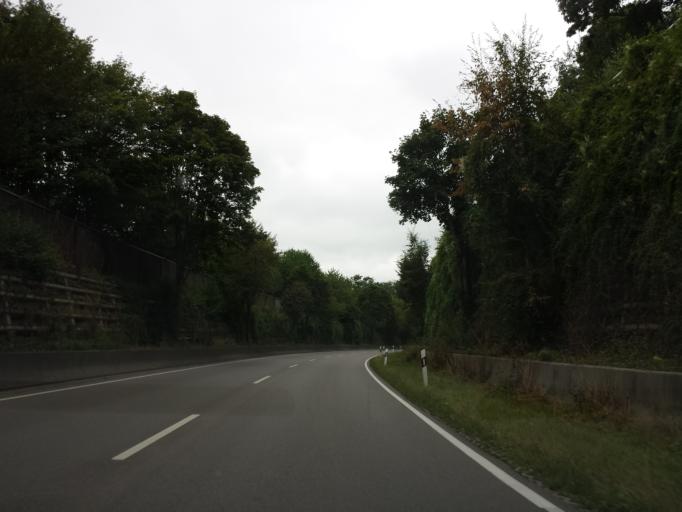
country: DE
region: Bavaria
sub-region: Swabia
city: Guenzburg
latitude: 48.4577
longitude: 10.2862
